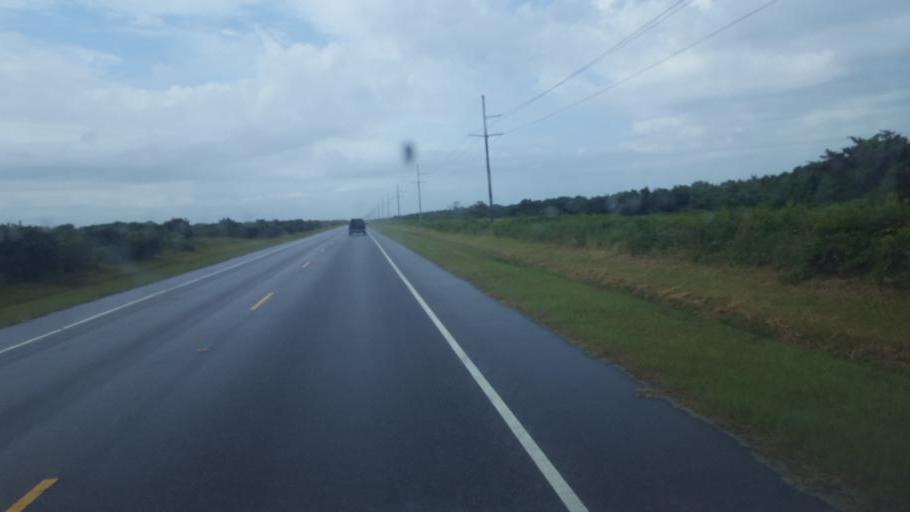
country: US
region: North Carolina
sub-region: Dare County
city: Buxton
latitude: 35.4834
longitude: -75.4818
